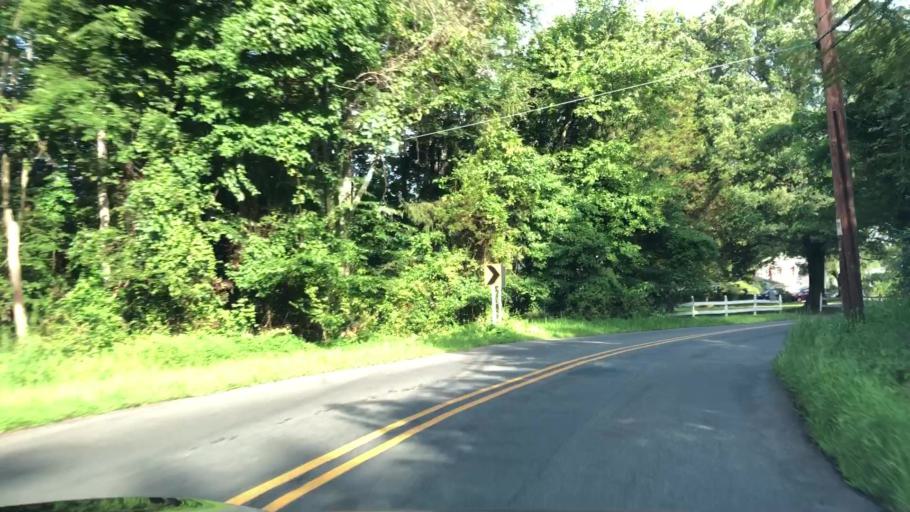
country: US
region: New Jersey
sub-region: Mercer County
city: Pennington
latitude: 40.3499
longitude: -74.7748
